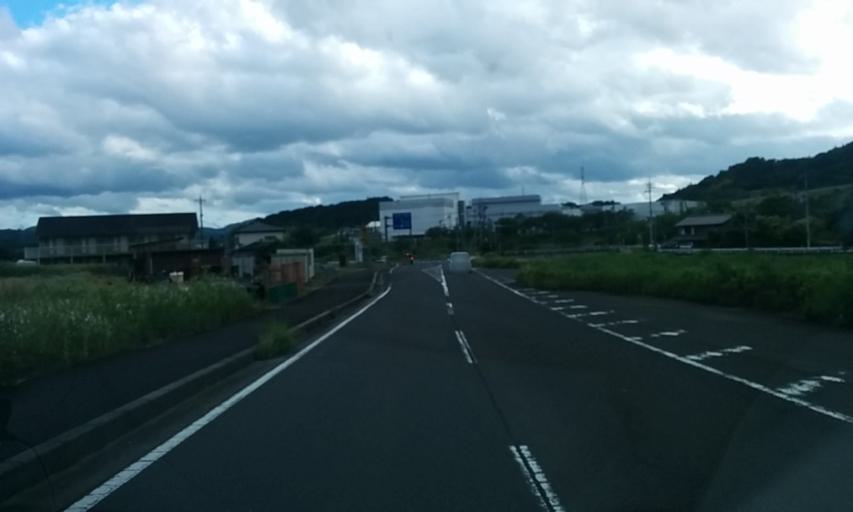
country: JP
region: Kyoto
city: Ayabe
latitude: 35.3353
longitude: 135.2934
